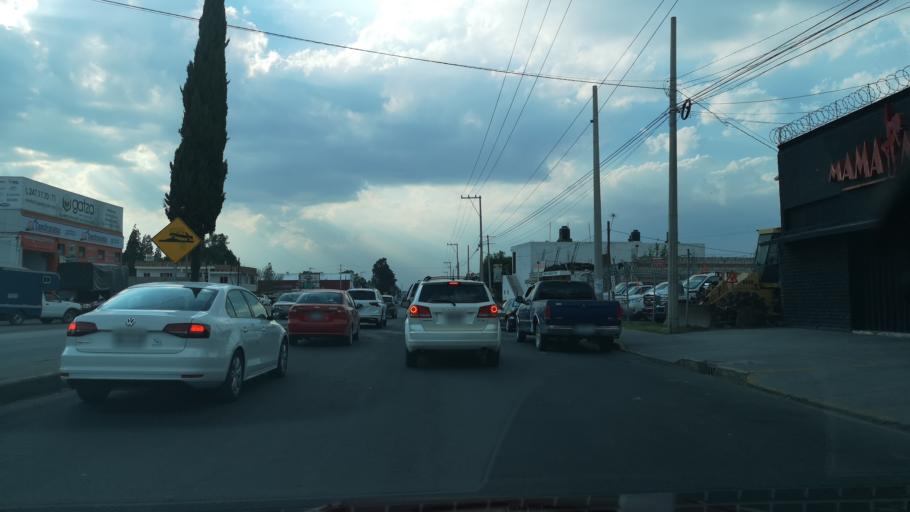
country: MX
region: Puebla
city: Cholula
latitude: 19.0728
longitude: -98.3169
